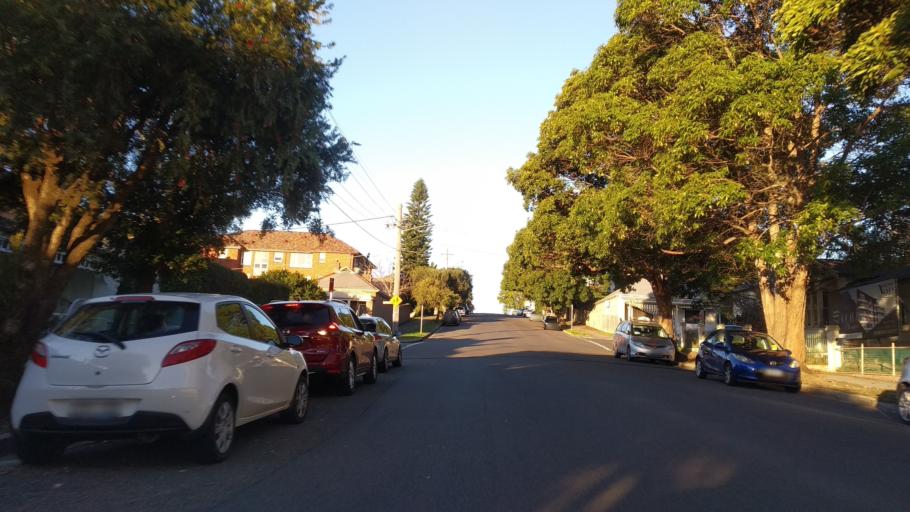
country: AU
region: New South Wales
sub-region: Rockdale
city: Banksia
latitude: -33.9510
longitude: 151.1407
